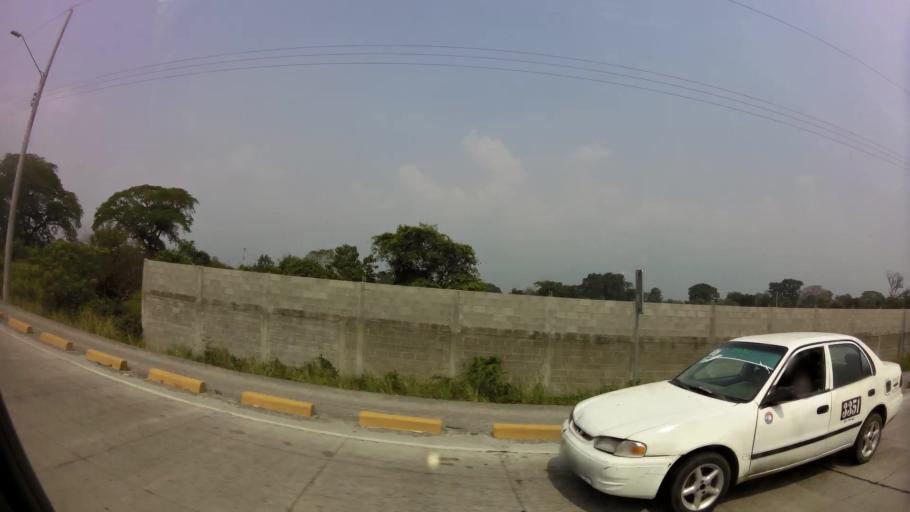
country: HN
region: Cortes
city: San Pedro Sula
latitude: 15.5192
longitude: -88.0019
